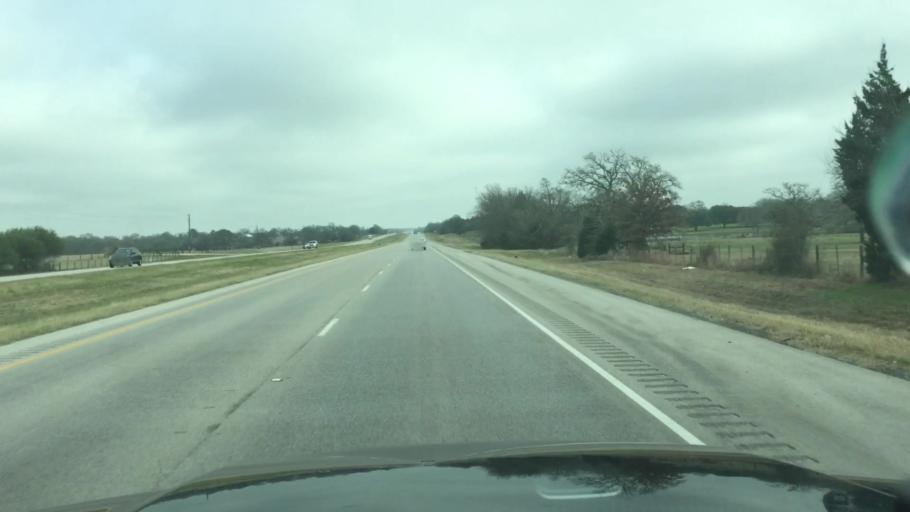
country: US
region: Texas
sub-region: Lee County
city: Giddings
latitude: 30.1451
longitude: -96.7233
